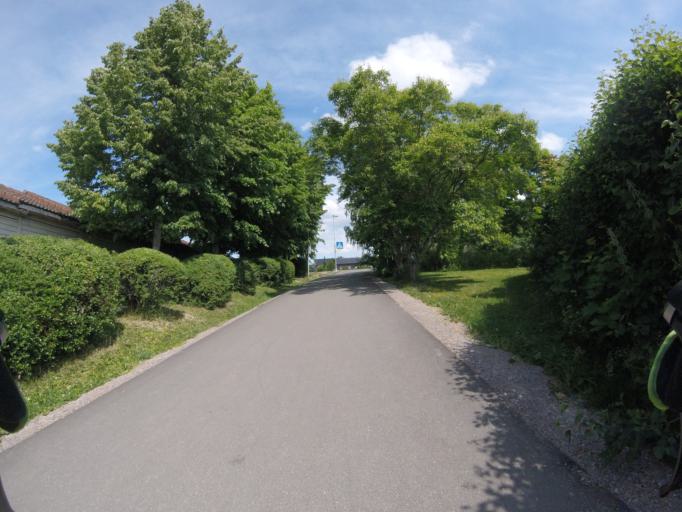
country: NO
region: Akershus
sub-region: Skedsmo
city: Lillestrom
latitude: 59.9911
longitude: 11.0362
